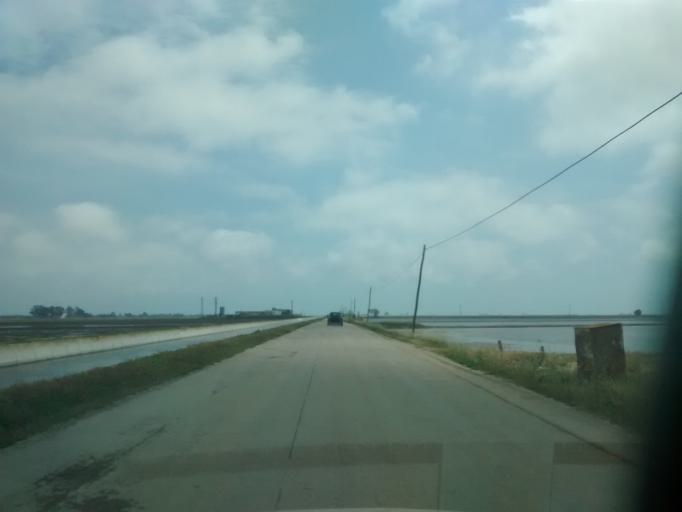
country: ES
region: Catalonia
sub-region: Provincia de Tarragona
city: Deltebre
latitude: 40.6999
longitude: 0.7481
